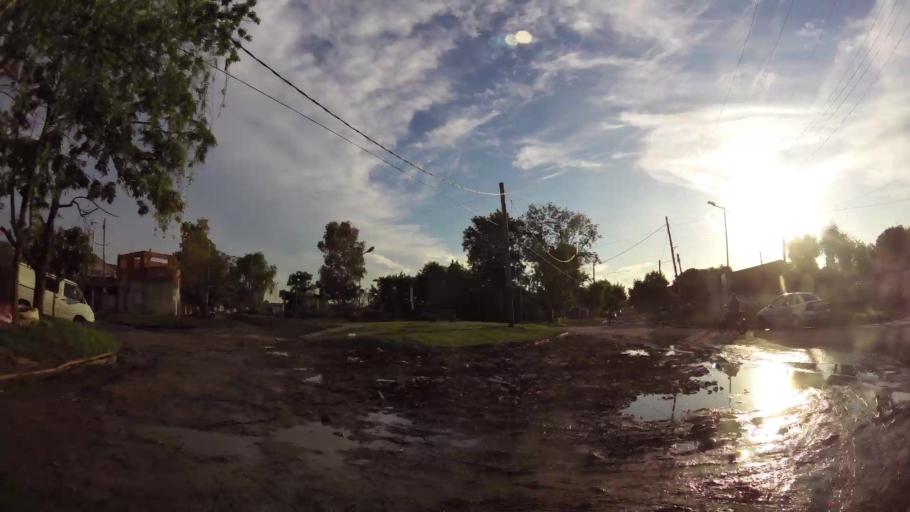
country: AR
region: Buenos Aires
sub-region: Partido de Lomas de Zamora
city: Lomas de Zamora
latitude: -34.7608
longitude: -58.3642
